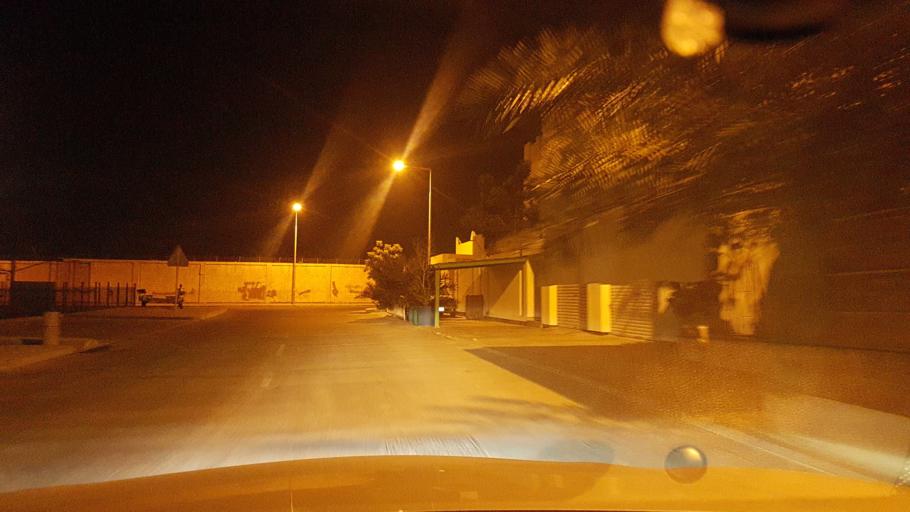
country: BH
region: Central Governorate
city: Madinat Hamad
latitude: 26.0965
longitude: 50.4793
